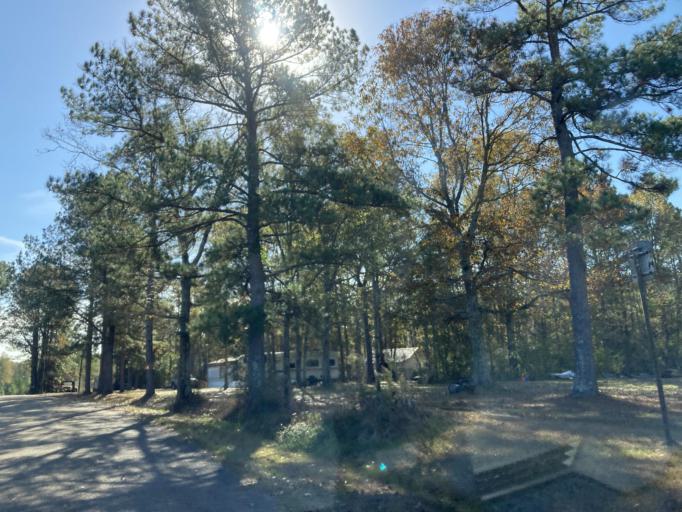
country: US
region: Mississippi
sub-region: Lamar County
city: Sumrall
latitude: 31.2671
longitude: -89.5304
